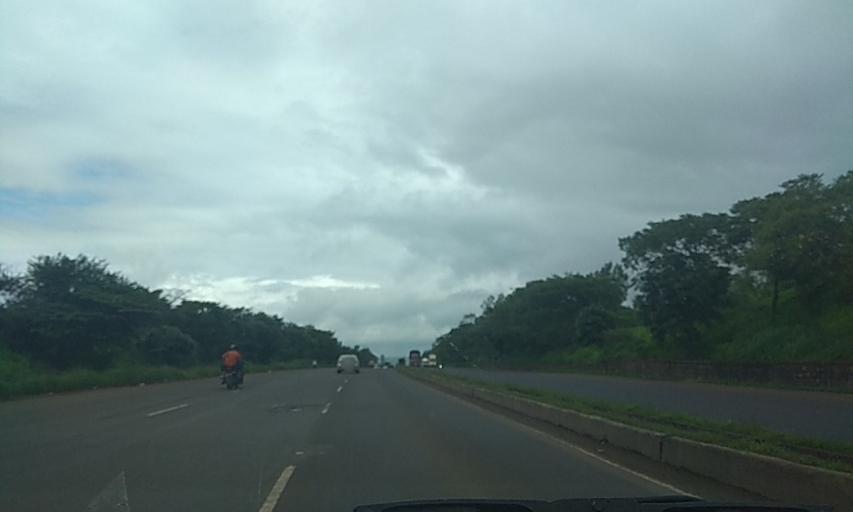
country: IN
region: Karnataka
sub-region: Belgaum
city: Belgaum
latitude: 15.8865
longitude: 74.5243
